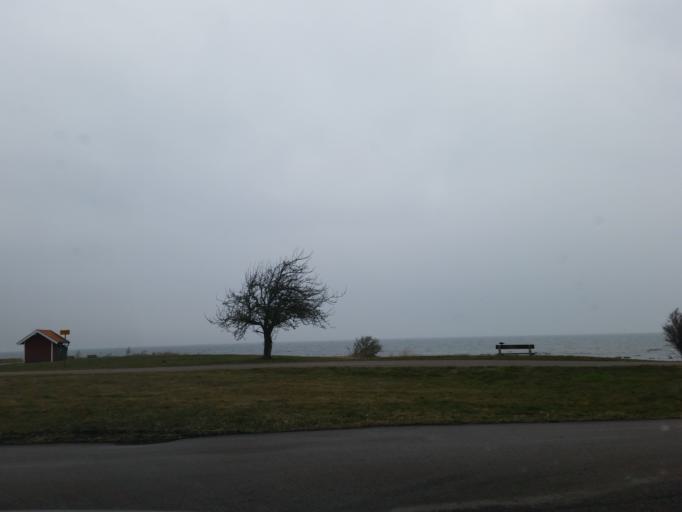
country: SE
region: Kalmar
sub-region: Morbylanga Kommun
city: Moerbylanga
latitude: 56.5235
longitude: 16.3715
